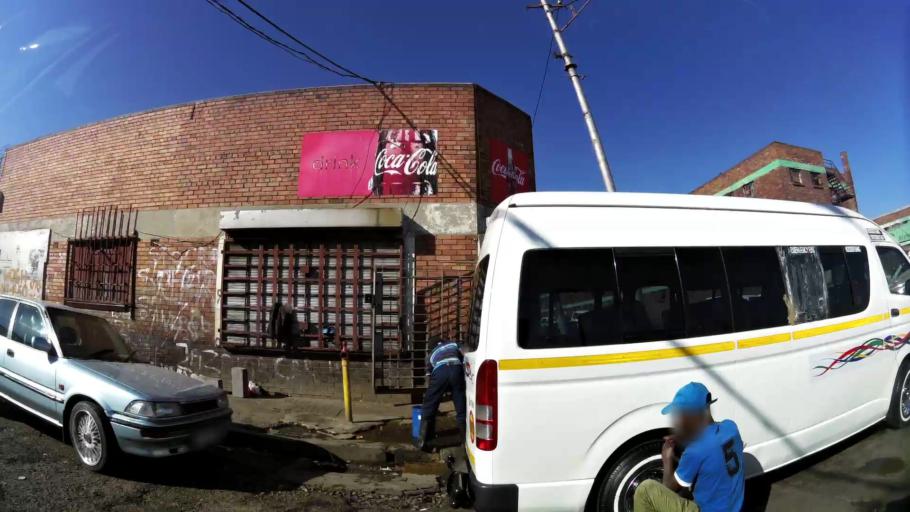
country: ZA
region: Gauteng
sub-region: City of Johannesburg Metropolitan Municipality
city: Johannesburg
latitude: -26.2088
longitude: 28.0661
